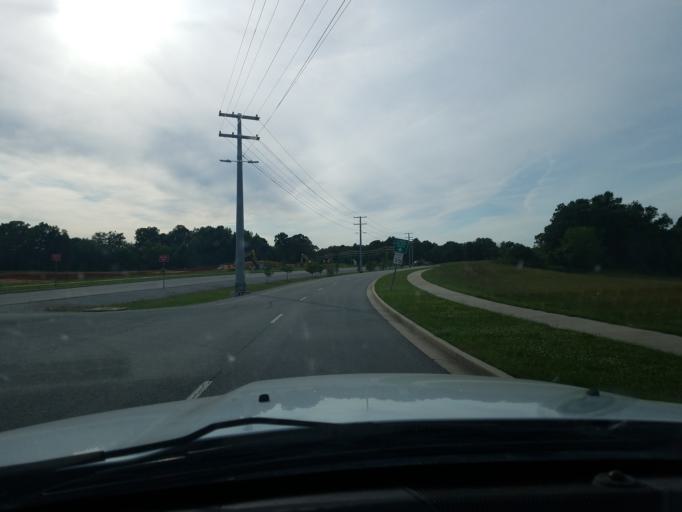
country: US
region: Tennessee
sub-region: Putnam County
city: Cookeville
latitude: 36.1297
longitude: -85.5504
